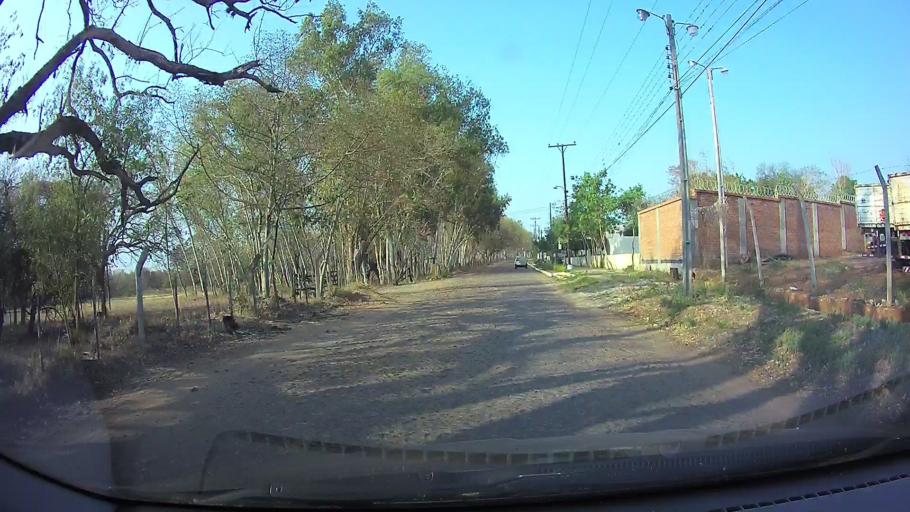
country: PY
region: Central
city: Limpio
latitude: -25.2248
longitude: -57.5074
